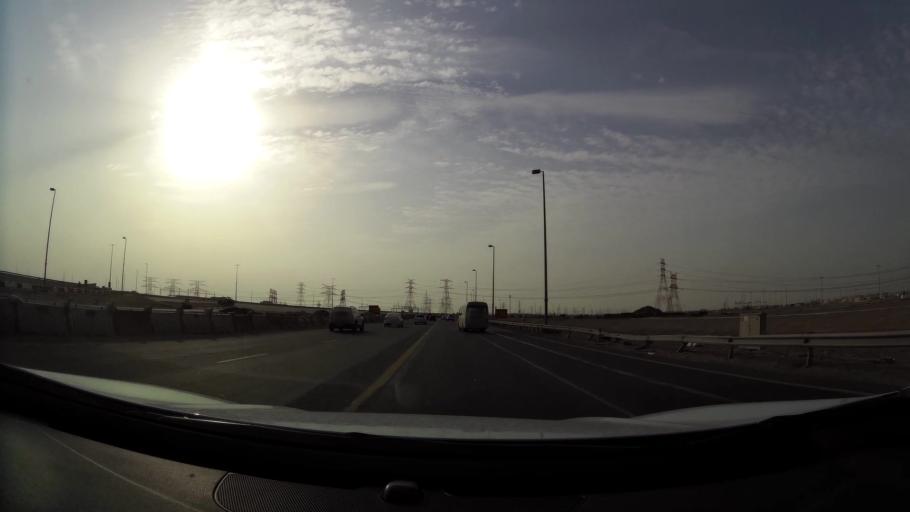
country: AE
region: Abu Dhabi
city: Abu Dhabi
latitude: 24.2936
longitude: 54.5498
